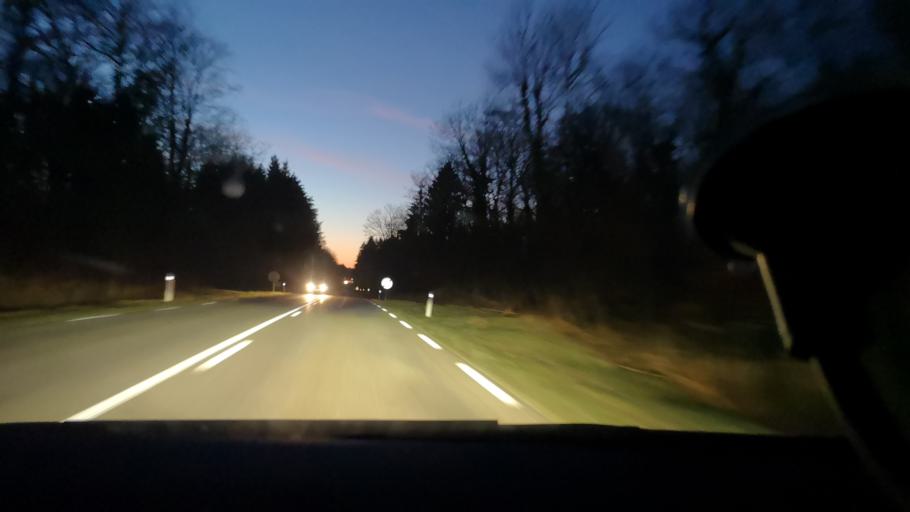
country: FR
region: Franche-Comte
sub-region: Departement du Jura
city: Poligny
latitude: 46.8159
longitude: 5.7643
